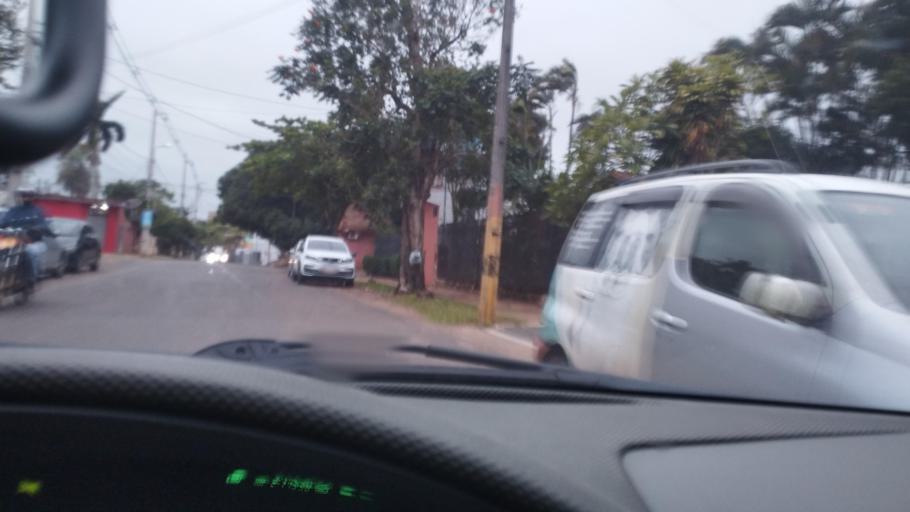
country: PY
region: Central
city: Fernando de la Mora
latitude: -25.3074
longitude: -57.5344
